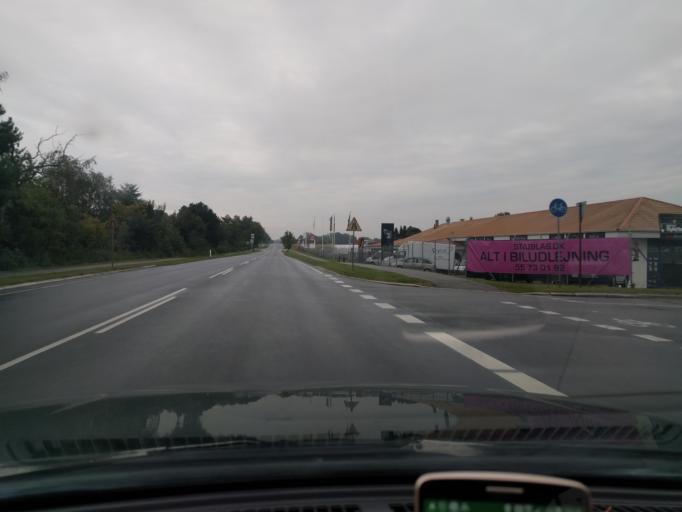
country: DK
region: Zealand
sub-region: Naestved Kommune
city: Naestved
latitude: 55.2003
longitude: 11.7603
